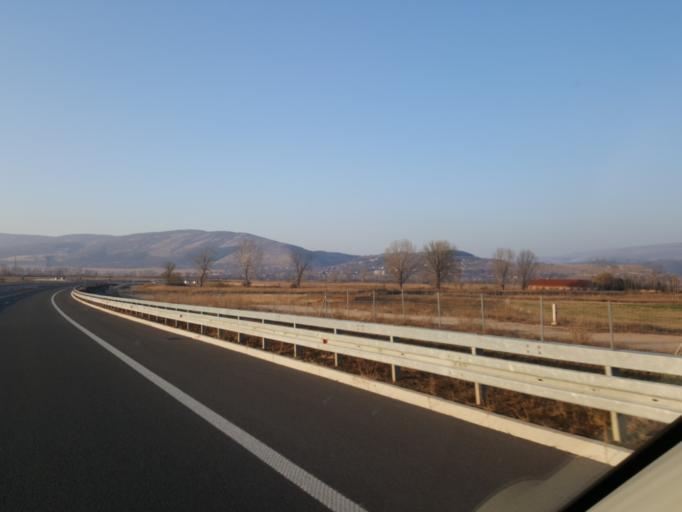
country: RS
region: Central Serbia
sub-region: Pirotski Okrug
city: Pirot
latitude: 43.1317
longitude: 22.5748
